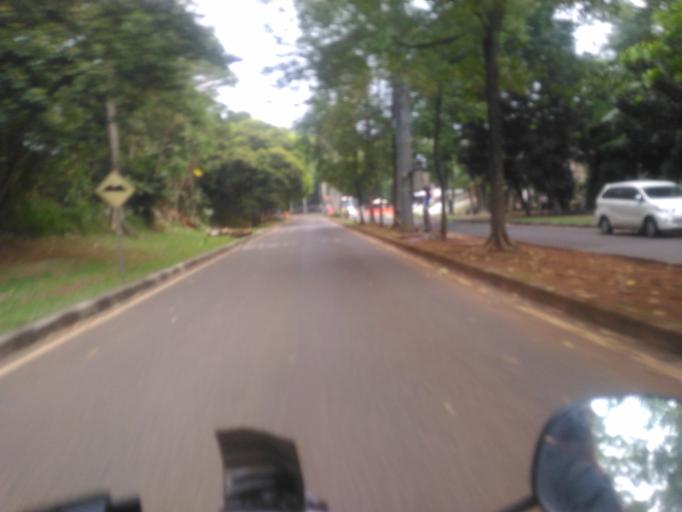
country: ID
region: West Java
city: Depok
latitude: -6.3502
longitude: 106.8318
